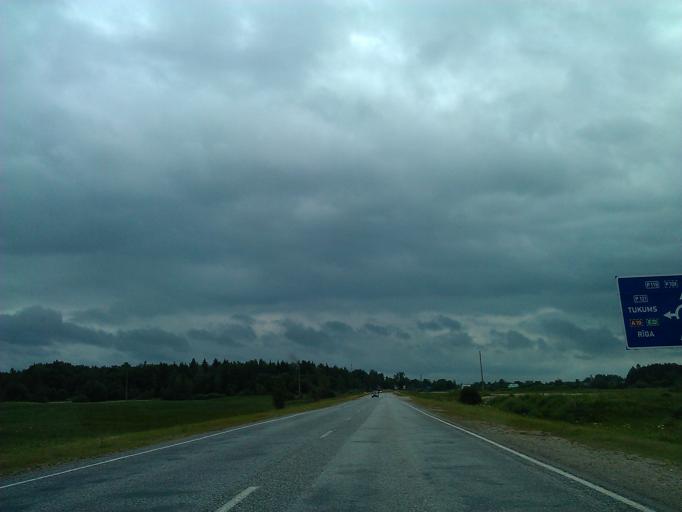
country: LV
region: Kuldigas Rajons
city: Kuldiga
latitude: 56.9761
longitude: 22.0160
